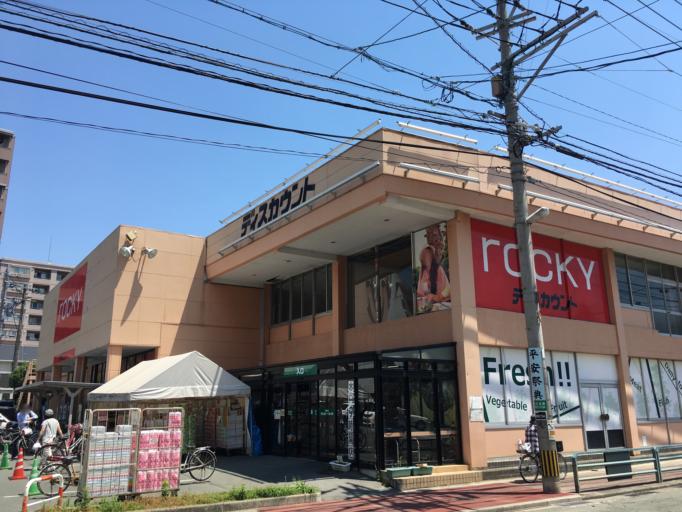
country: JP
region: Kumamoto
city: Kumamoto
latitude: 32.7924
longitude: 130.7326
